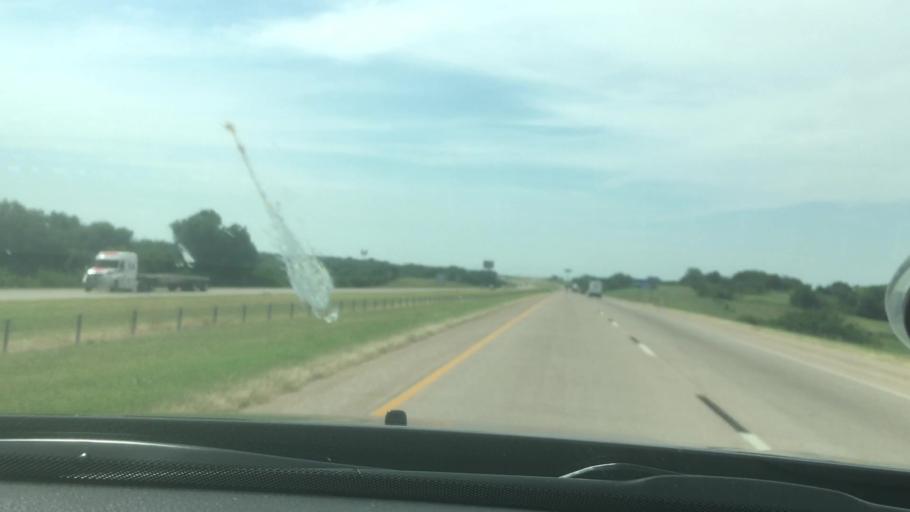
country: US
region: Oklahoma
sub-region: Garvin County
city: Pauls Valley
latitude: 34.7226
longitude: -97.2533
